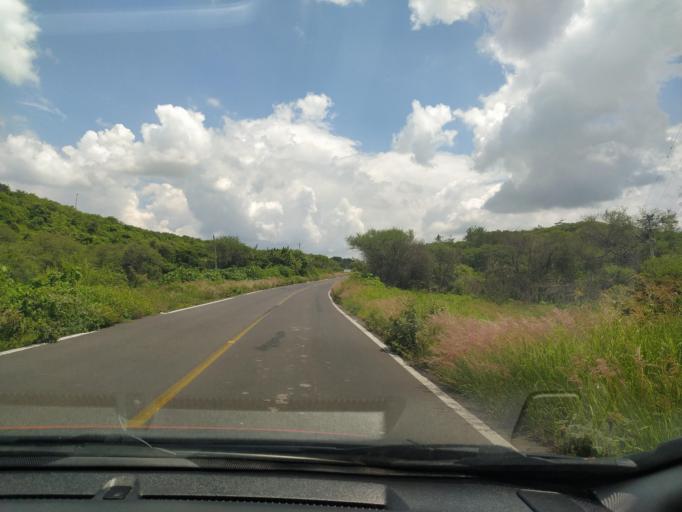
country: MX
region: Jalisco
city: Villa Corona
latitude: 20.4047
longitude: -103.6832
